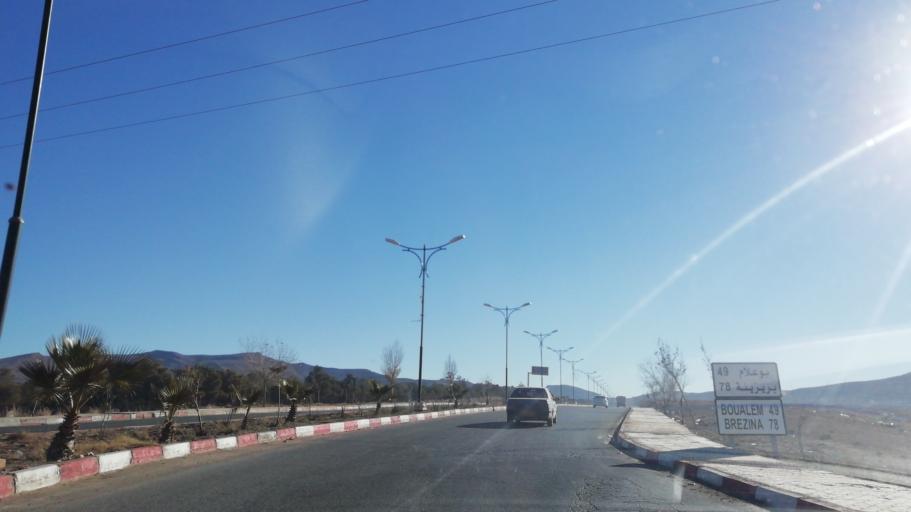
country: DZ
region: El Bayadh
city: El Bayadh
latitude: 33.6612
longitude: 1.0570
